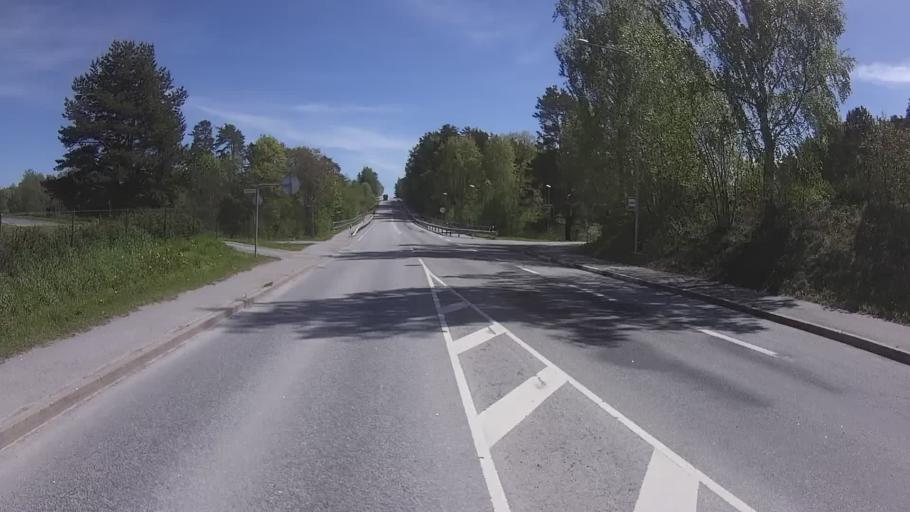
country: EE
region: Vorumaa
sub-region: Voru linn
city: Voru
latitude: 57.8133
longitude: 27.0438
